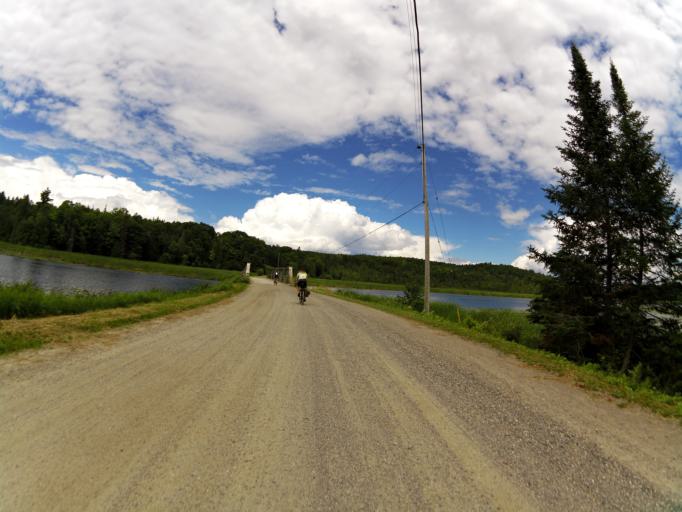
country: CA
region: Ontario
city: Renfrew
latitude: 45.1332
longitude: -76.6731
